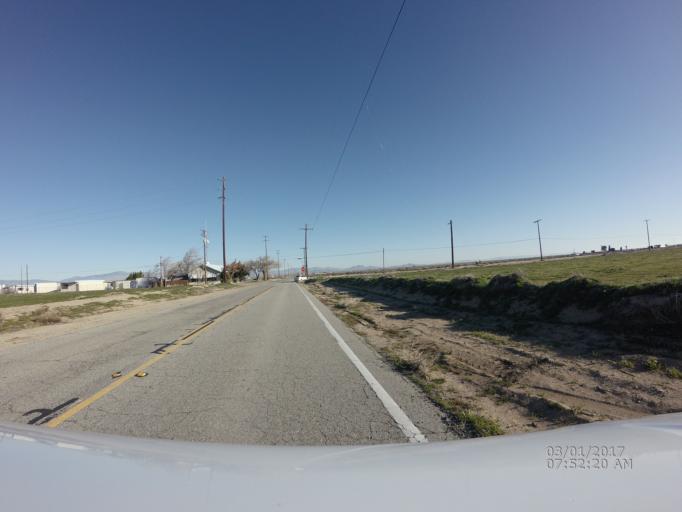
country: US
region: California
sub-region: Los Angeles County
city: Quartz Hill
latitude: 34.7325
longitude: -118.2549
